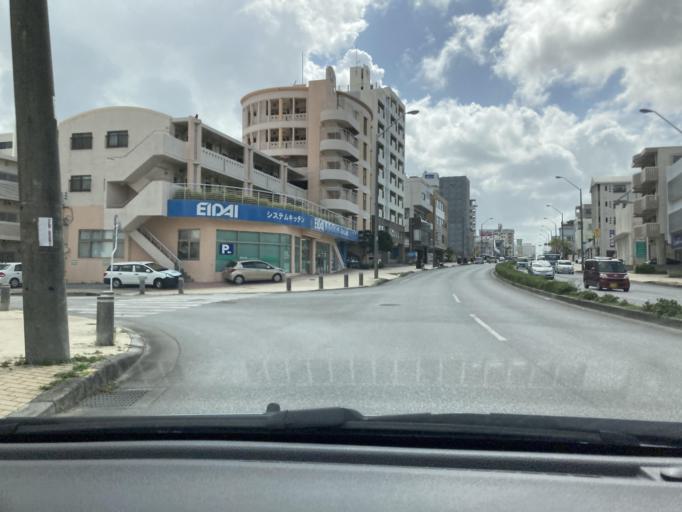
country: JP
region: Okinawa
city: Naha-shi
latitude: 26.2324
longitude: 127.7023
